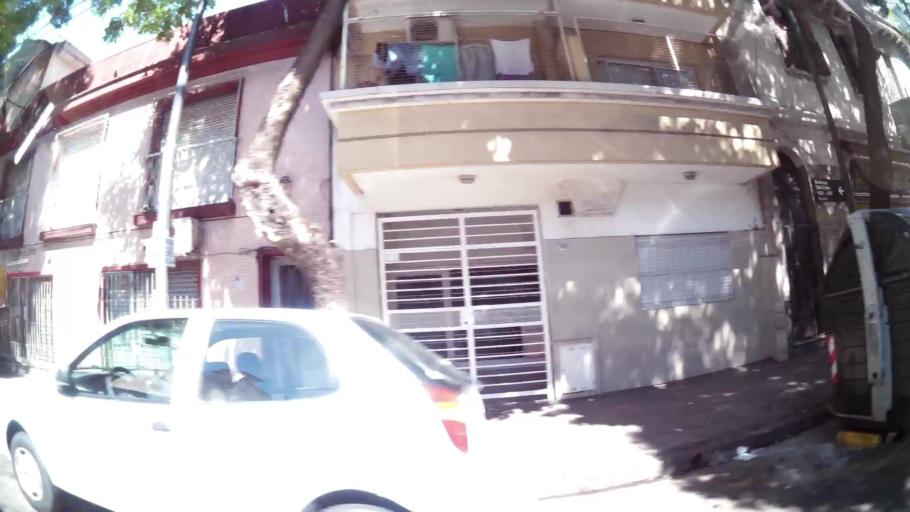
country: AR
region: Buenos Aires F.D.
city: Buenos Aires
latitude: -34.6263
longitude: -58.3843
